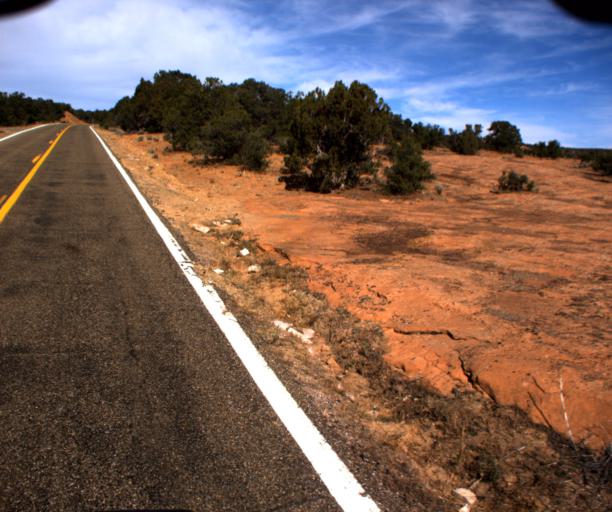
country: US
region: Arizona
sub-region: Navajo County
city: Kayenta
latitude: 36.6184
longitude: -110.5056
